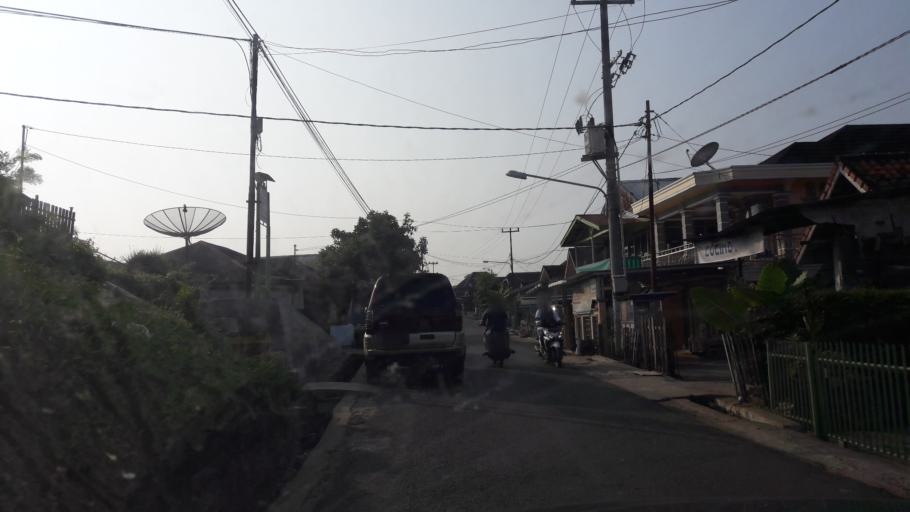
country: ID
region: South Sumatra
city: Gunungmegang Dalam
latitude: -3.2735
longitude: 103.8265
